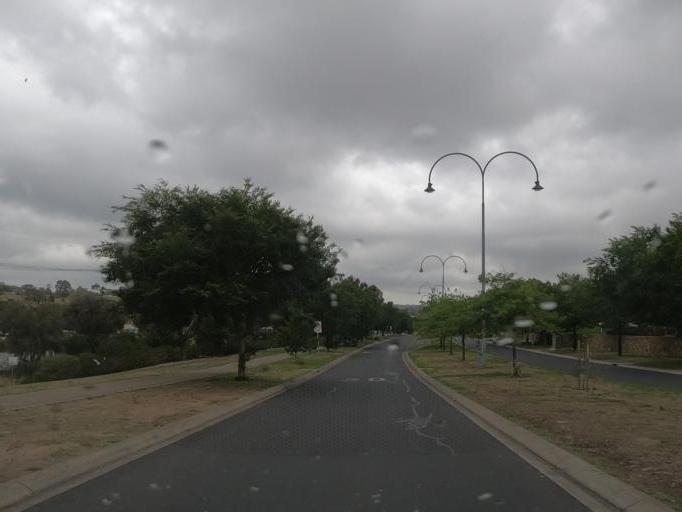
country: AU
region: Victoria
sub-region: Hume
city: Meadow Heights
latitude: -37.6385
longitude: 144.9091
